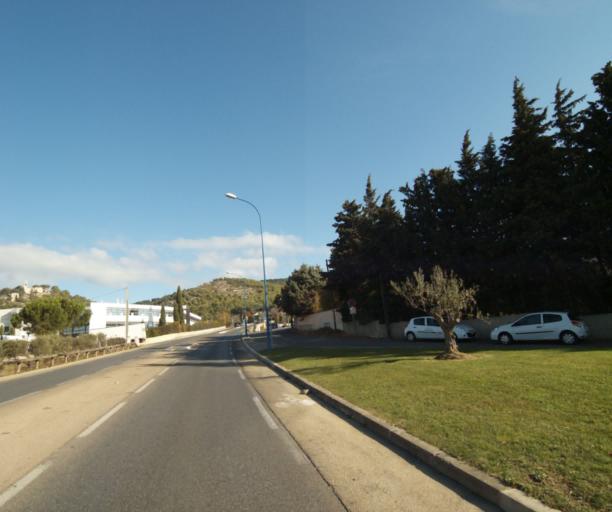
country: FR
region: Provence-Alpes-Cote d'Azur
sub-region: Departement des Bouches-du-Rhone
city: Allauch
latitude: 43.3299
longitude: 5.4846
